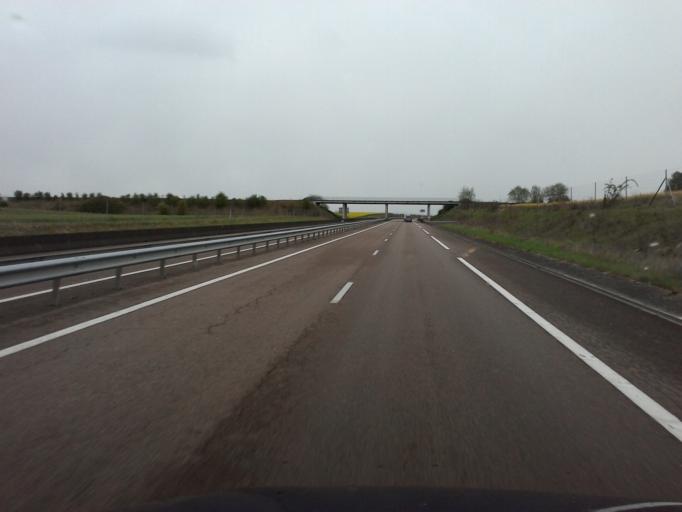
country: FR
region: Champagne-Ardenne
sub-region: Departement de la Haute-Marne
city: Chaumont
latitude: 48.1407
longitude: 5.1140
